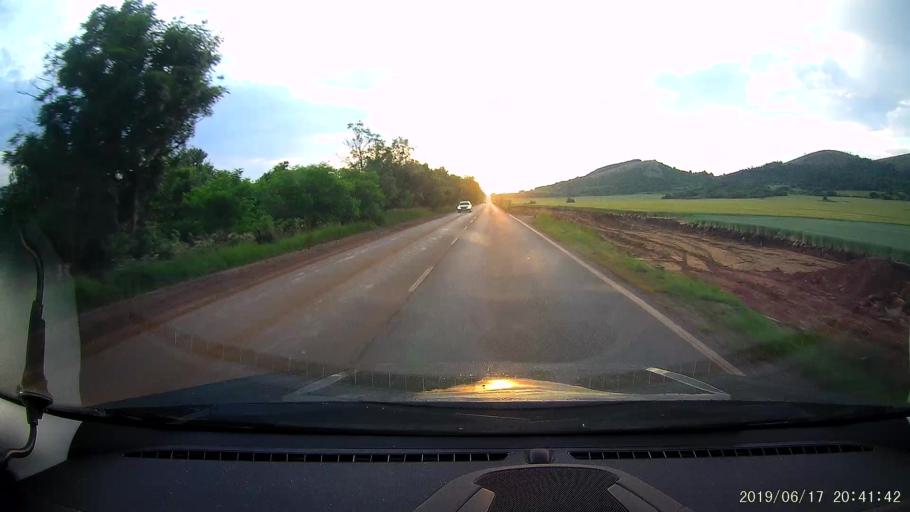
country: BG
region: Sofiya
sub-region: Obshtina Dragoman
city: Dragoman
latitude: 42.8969
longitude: 22.9640
